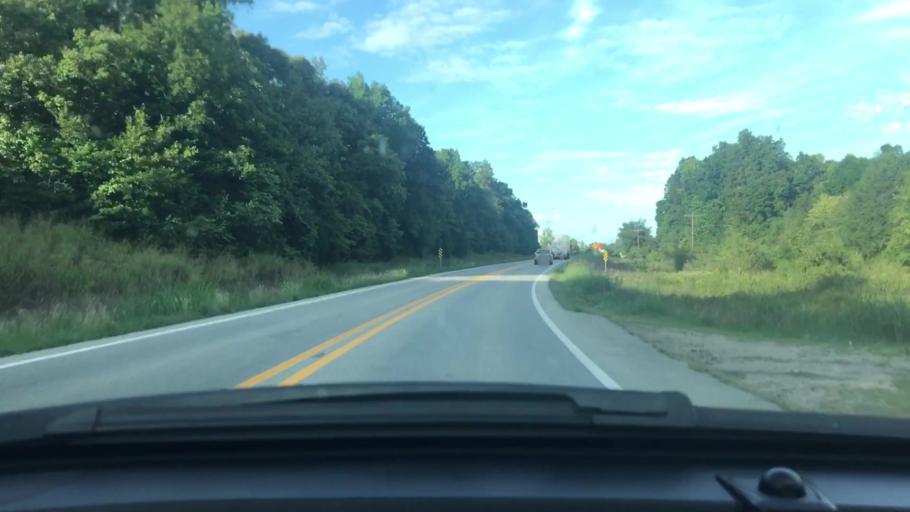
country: US
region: Arkansas
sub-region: Sharp County
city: Cherokee Village
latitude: 36.2996
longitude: -91.4320
